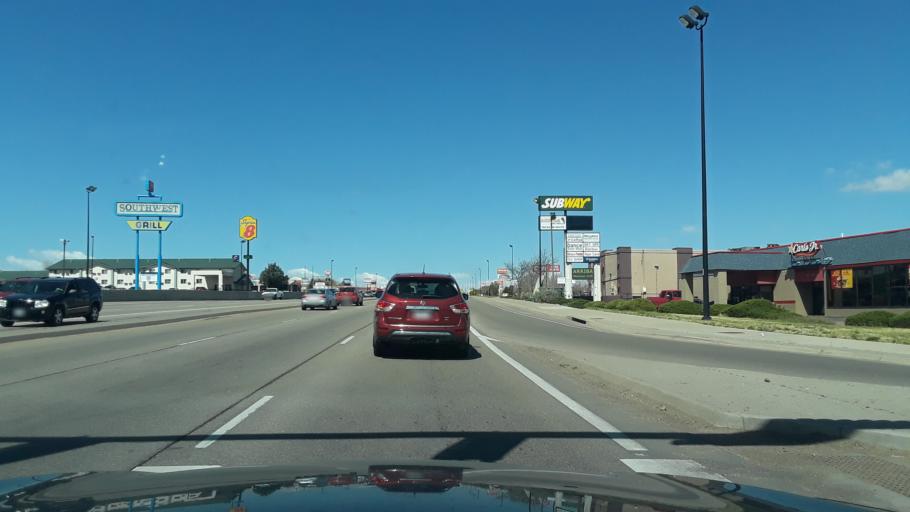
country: US
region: Colorado
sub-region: Pueblo County
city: Pueblo
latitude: 38.3082
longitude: -104.6206
